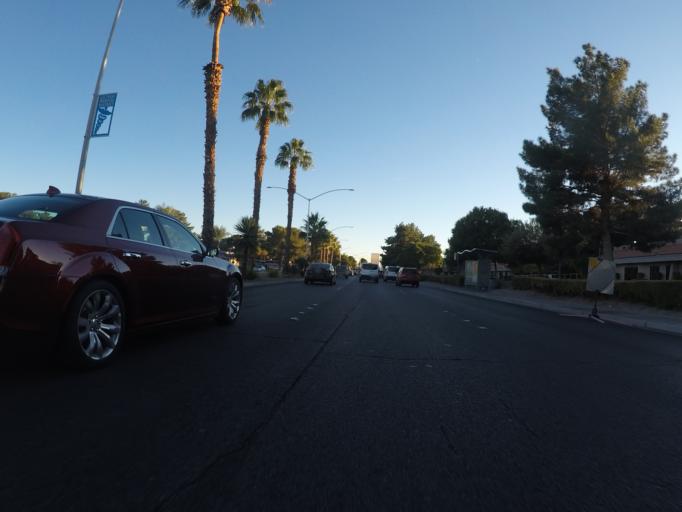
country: US
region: Nevada
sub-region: Clark County
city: Las Vegas
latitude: 36.1659
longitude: -115.1728
